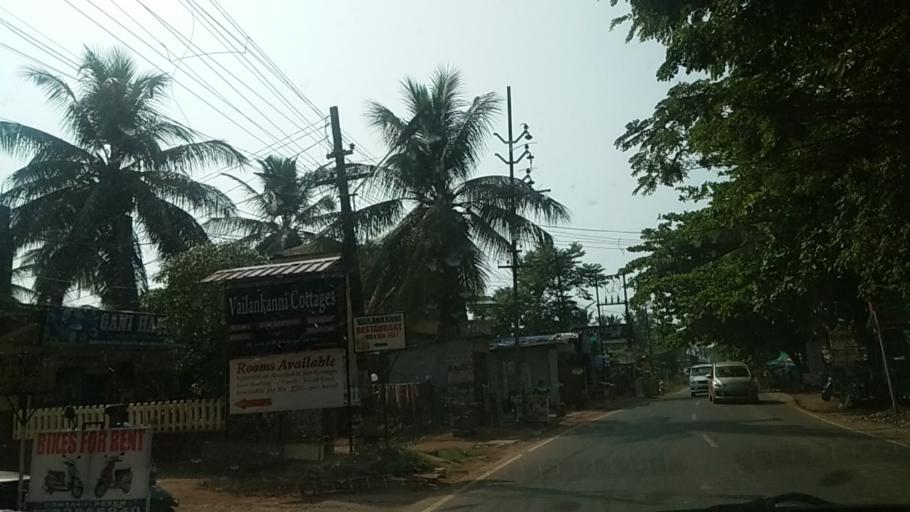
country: IN
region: Goa
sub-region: South Goa
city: Colva
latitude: 15.2764
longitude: 73.9187
